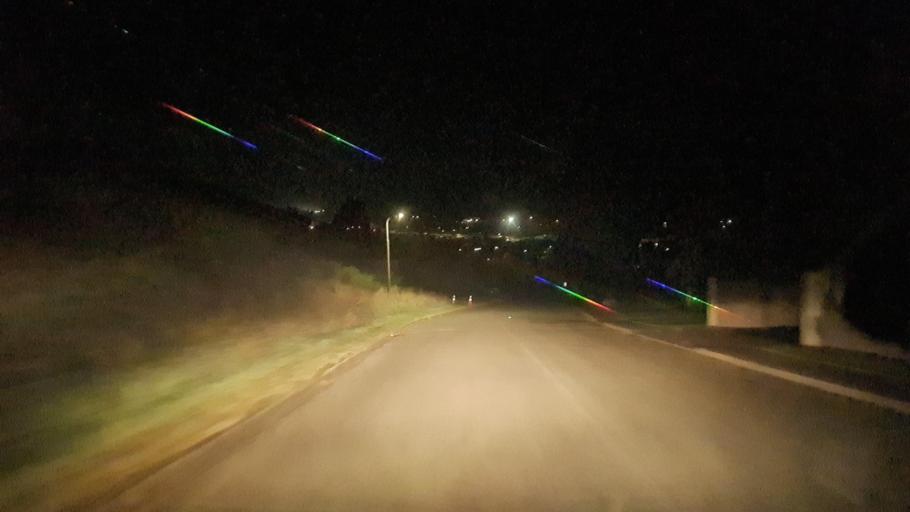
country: NZ
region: Otago
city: Oamaru
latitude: -45.0790
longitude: 170.9740
